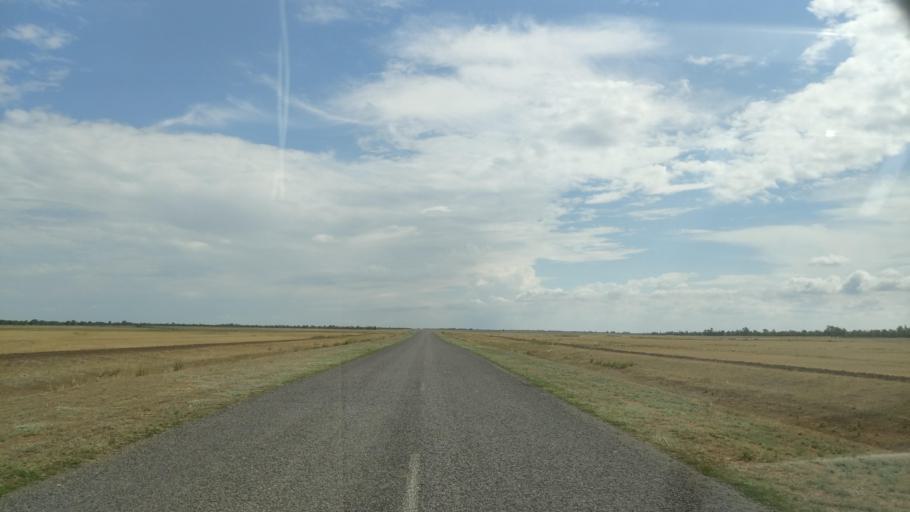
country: KZ
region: Pavlodar
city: Pavlodar
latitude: 52.6354
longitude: 76.9053
